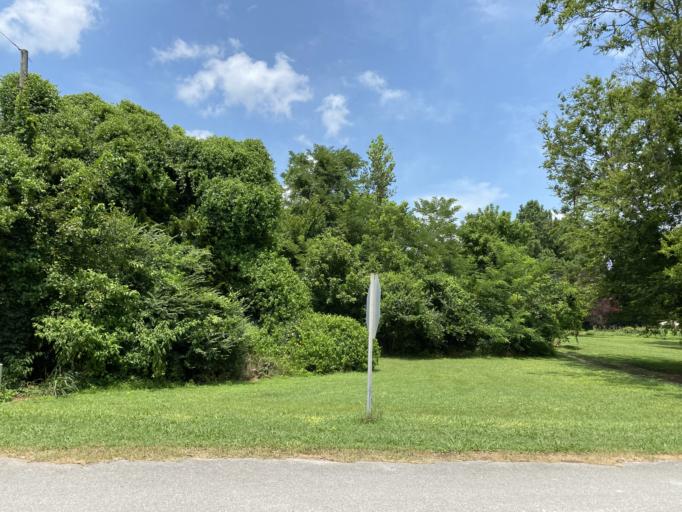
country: US
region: Alabama
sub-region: Lawrence County
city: Town Creek
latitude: 34.6690
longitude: -87.3021
